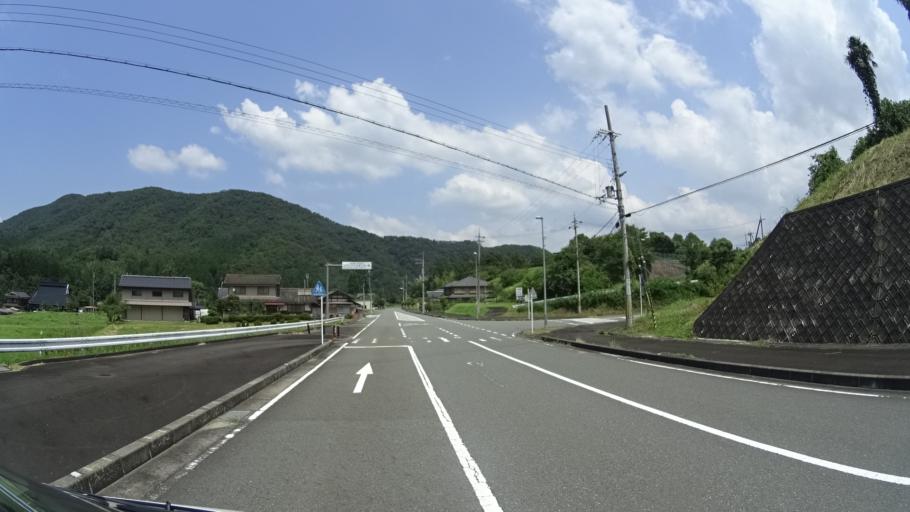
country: JP
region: Kyoto
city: Ayabe
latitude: 35.2205
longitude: 135.2156
